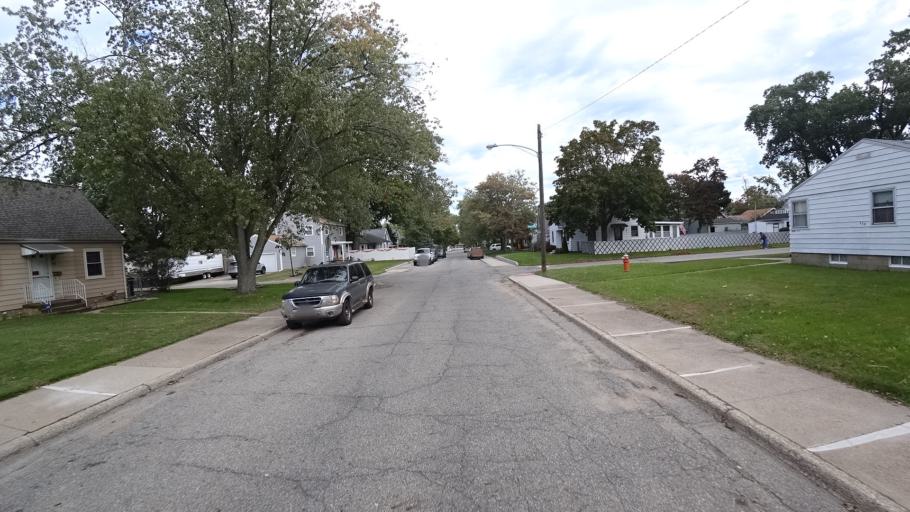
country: US
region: Indiana
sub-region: LaPorte County
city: Michigan City
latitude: 41.7079
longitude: -86.8773
